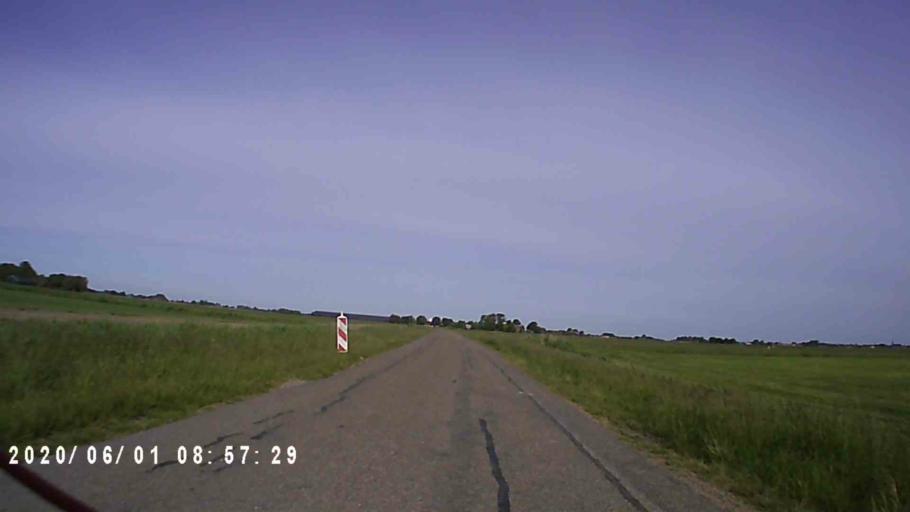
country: NL
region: Friesland
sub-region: Gemeente Leeuwarderadeel
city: Britsum
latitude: 53.2806
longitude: 5.8123
